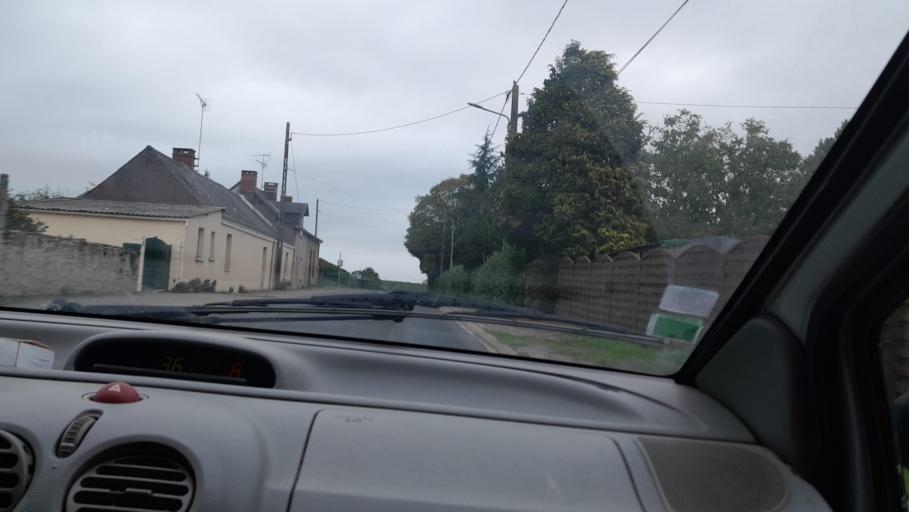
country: FR
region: Pays de la Loire
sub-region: Departement de Maine-et-Loire
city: Pouance
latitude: 47.6795
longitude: -1.1832
